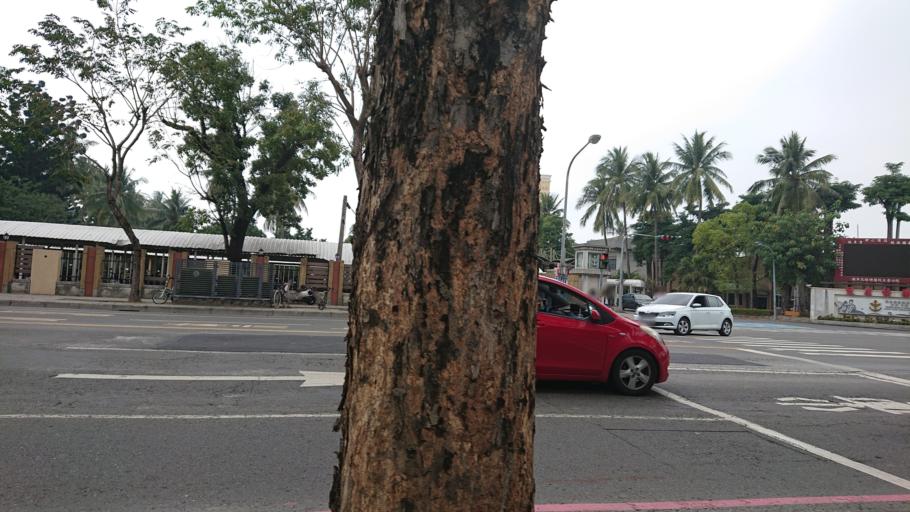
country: TW
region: Kaohsiung
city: Kaohsiung
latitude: 22.7012
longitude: 120.2926
